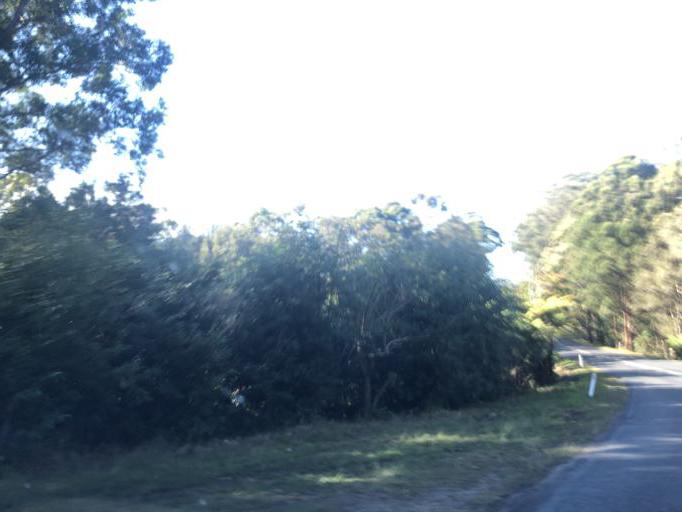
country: AU
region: New South Wales
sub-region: Coffs Harbour
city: Toormina
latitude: -30.3479
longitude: 153.0861
